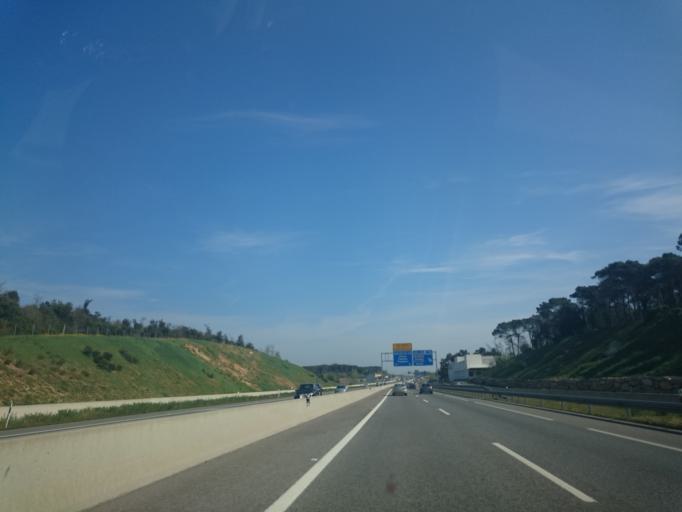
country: ES
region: Catalonia
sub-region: Provincia de Girona
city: Riudellots de la Selva
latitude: 41.9104
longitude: 2.7901
